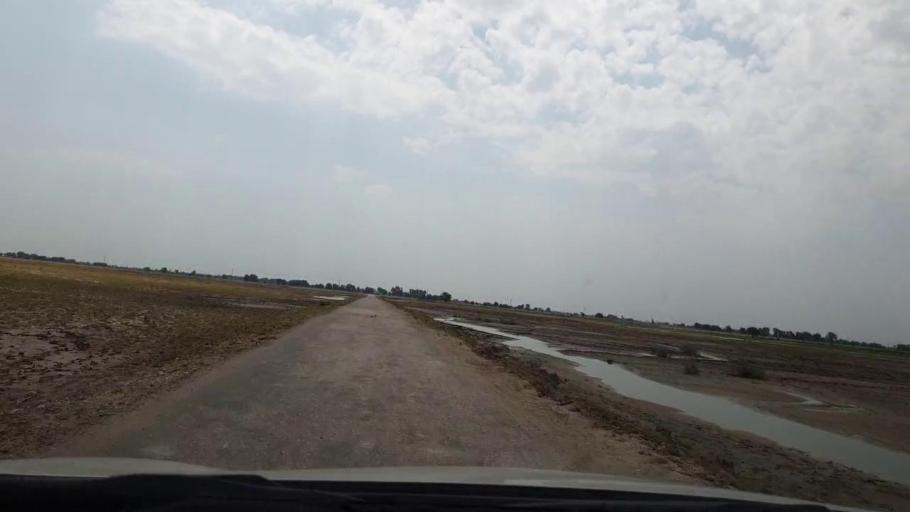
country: PK
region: Sindh
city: Ratodero
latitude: 27.8374
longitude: 68.3013
